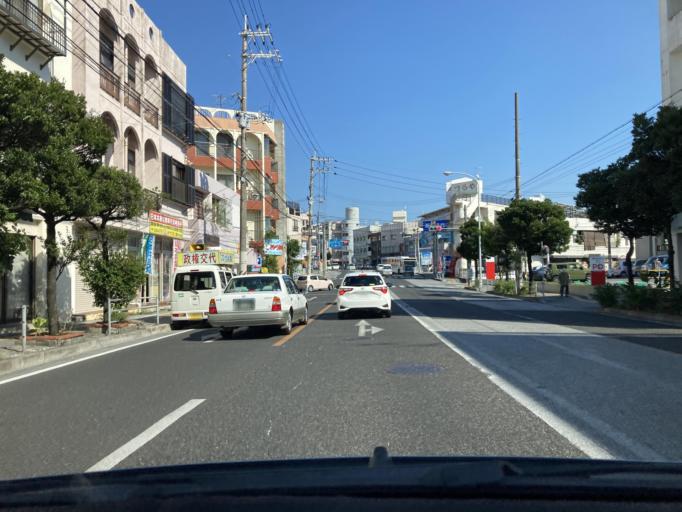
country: JP
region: Okinawa
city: Naha-shi
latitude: 26.2058
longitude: 127.6973
